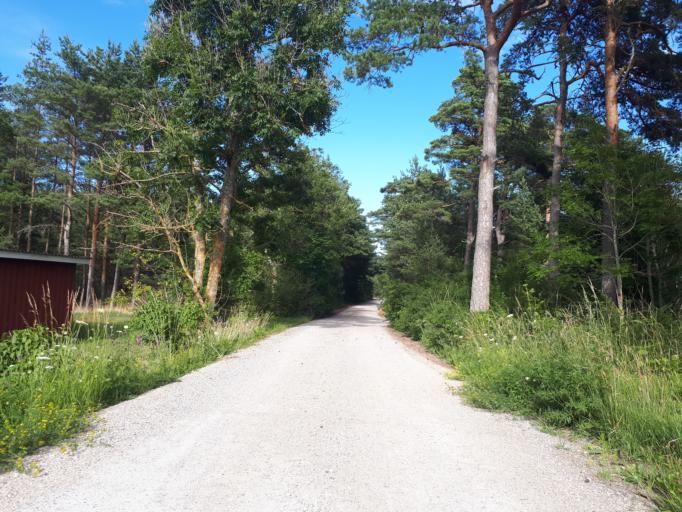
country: SE
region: Gotland
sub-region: Gotland
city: Vibble
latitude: 57.6052
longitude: 18.2859
